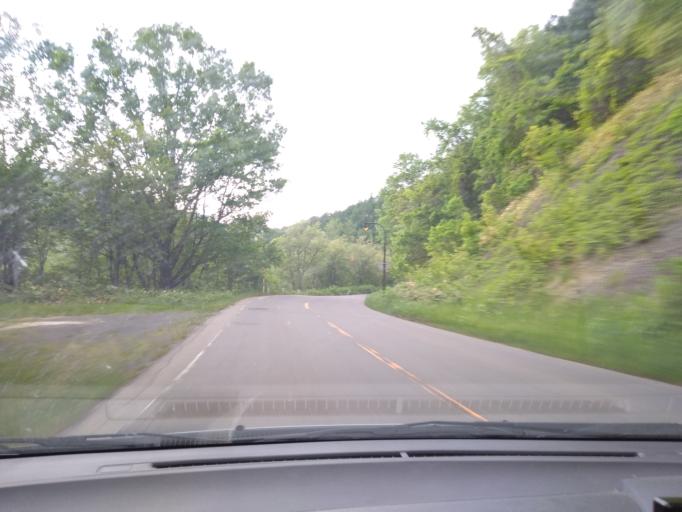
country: JP
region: Hokkaido
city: Shimo-furano
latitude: 43.1456
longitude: 142.4790
